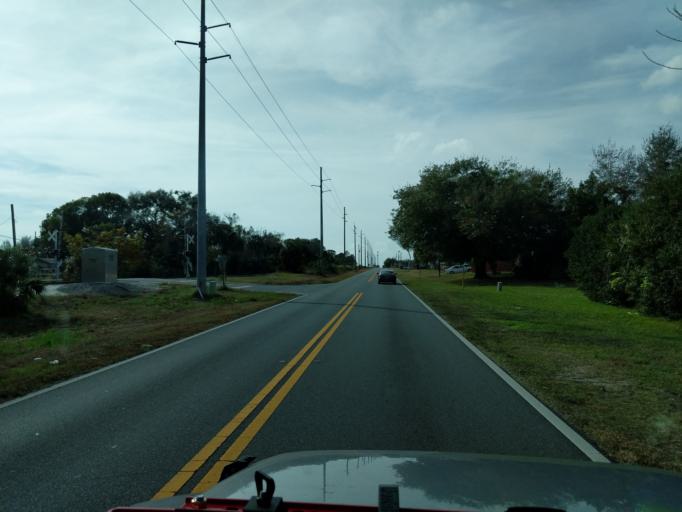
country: US
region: Florida
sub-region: Lake County
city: Mount Dora
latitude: 28.8070
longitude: -81.6772
